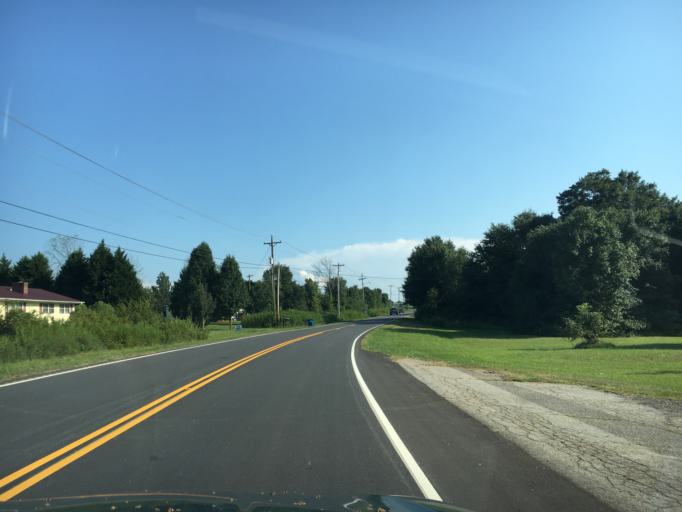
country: US
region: South Carolina
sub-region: Spartanburg County
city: Duncan
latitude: 34.9245
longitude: -82.1440
